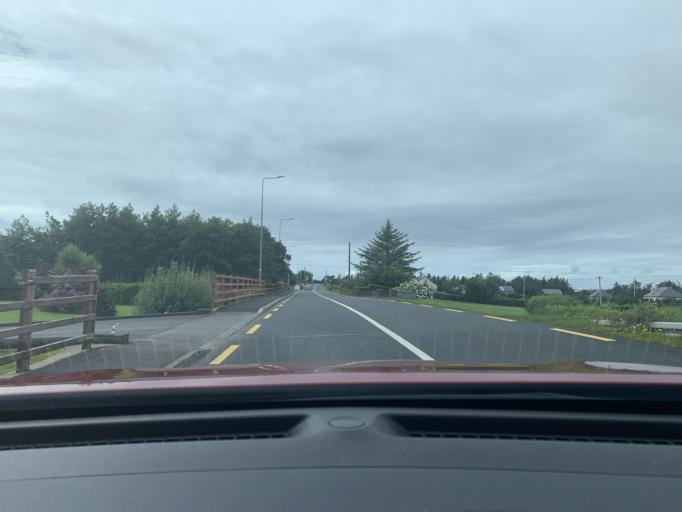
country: IE
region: Ulster
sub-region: County Donegal
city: Dungloe
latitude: 54.9505
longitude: -8.3416
